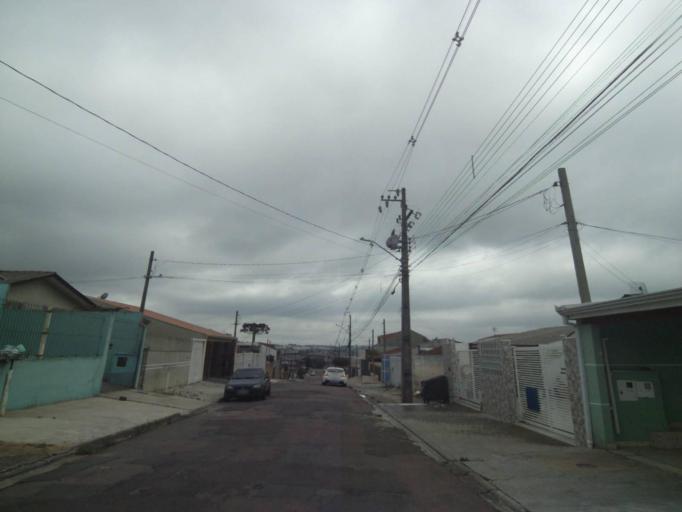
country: BR
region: Parana
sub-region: Curitiba
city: Curitiba
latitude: -25.4824
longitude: -49.3542
